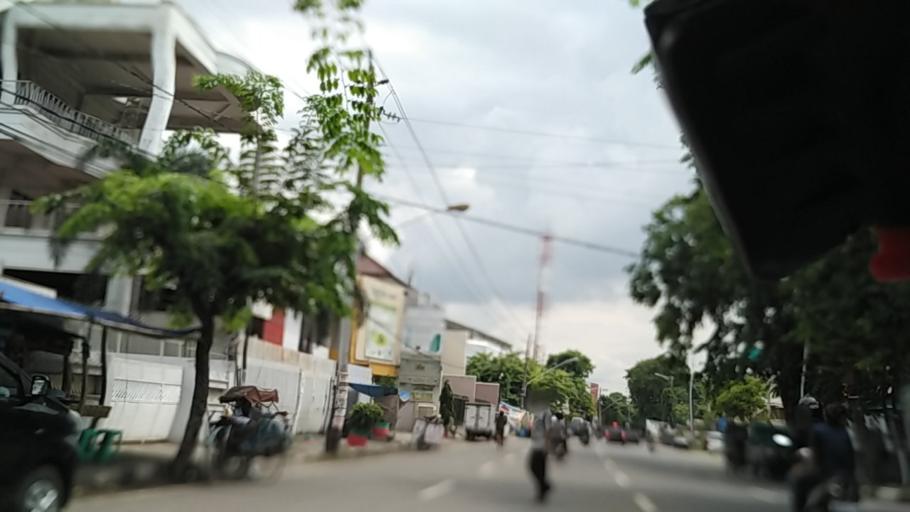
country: ID
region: Central Java
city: Semarang
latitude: -6.9765
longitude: 110.4351
